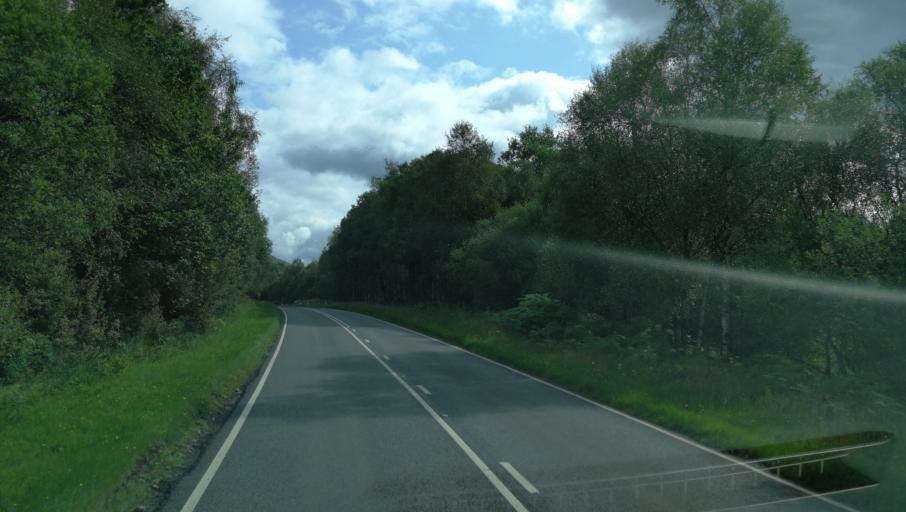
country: GB
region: Scotland
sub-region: Highland
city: Fort William
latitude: 56.8584
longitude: -5.3585
